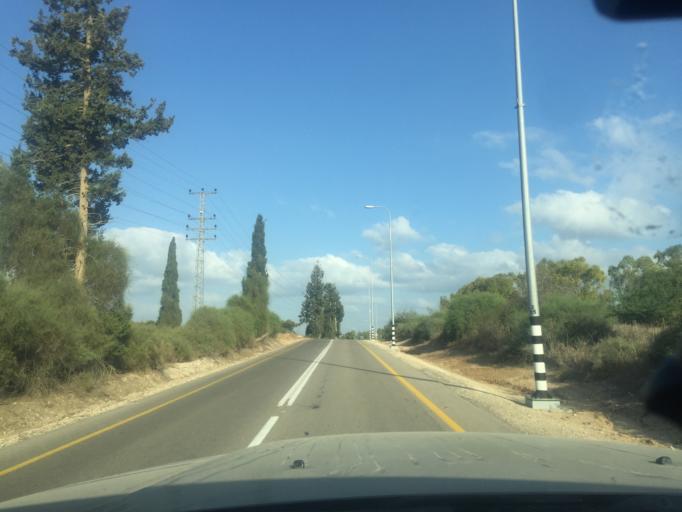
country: PS
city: Umm an Nasr
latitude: 31.6037
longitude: 34.5676
